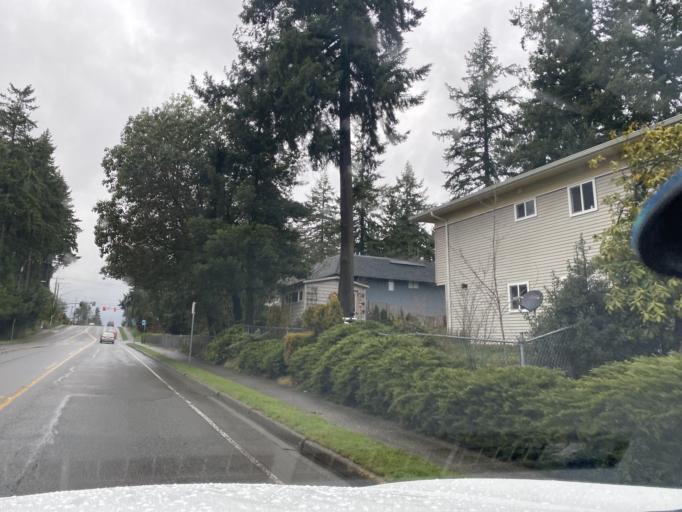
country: US
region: Washington
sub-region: Snohomish County
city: Mountlake Terrace
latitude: 47.7993
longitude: -122.3059
